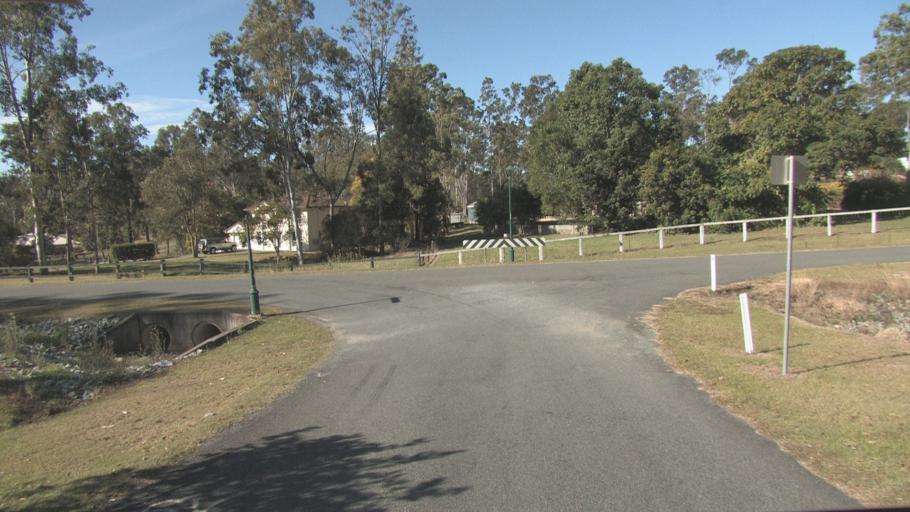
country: AU
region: Queensland
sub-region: Ipswich
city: Springfield Lakes
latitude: -27.7321
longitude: 152.9286
